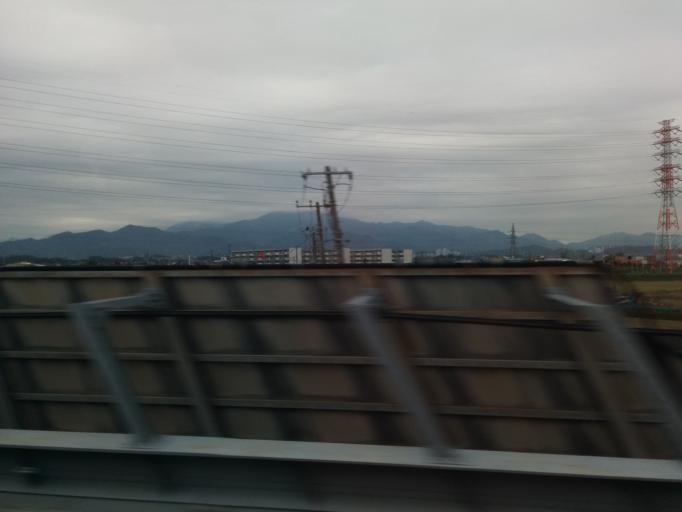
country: JP
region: Kanagawa
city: Isehara
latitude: 35.3764
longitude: 139.3492
